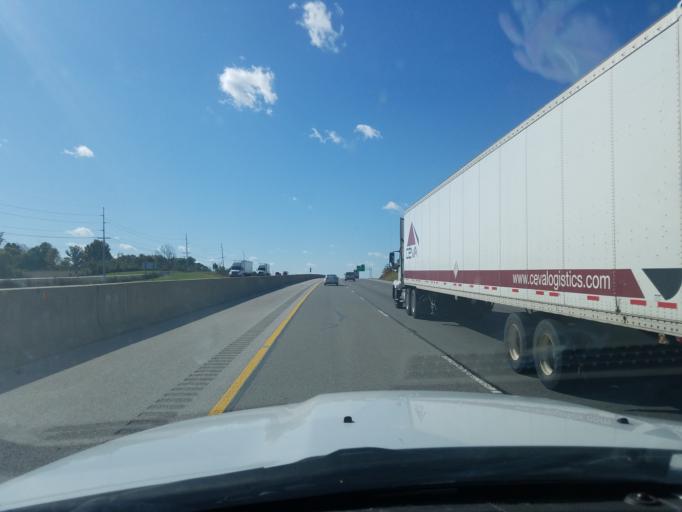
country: US
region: Kentucky
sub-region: Warren County
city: Bowling Green
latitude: 36.9664
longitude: -86.3972
